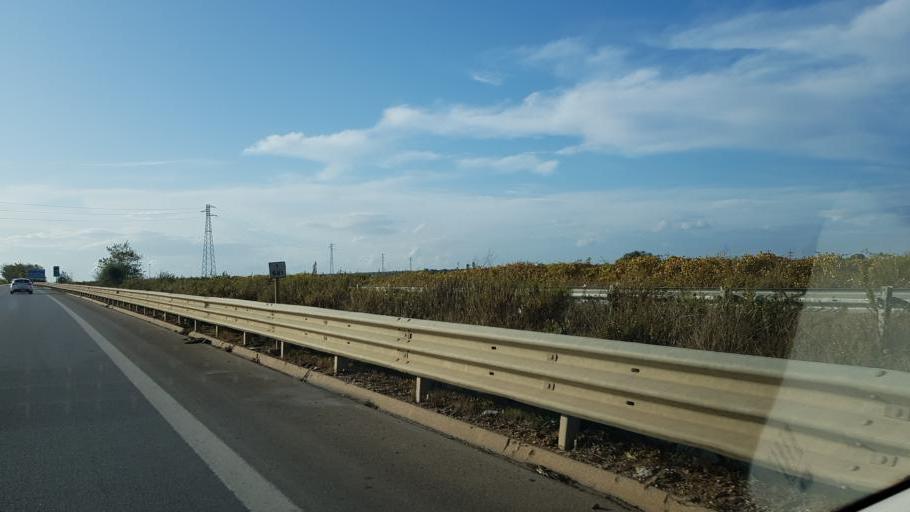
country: IT
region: Apulia
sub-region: Provincia di Brindisi
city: Francavilla Fontana
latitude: 40.5465
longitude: 17.5833
